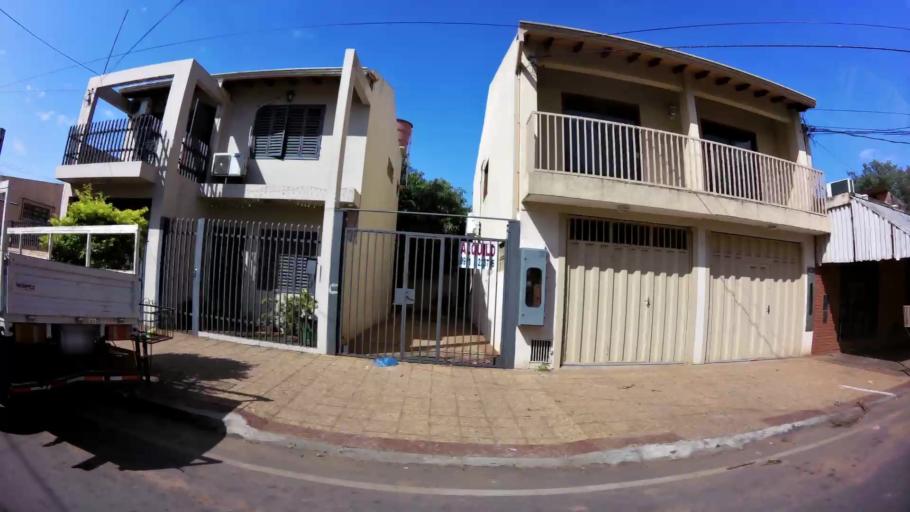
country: PY
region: Central
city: San Lorenzo
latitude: -25.3512
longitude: -57.5105
